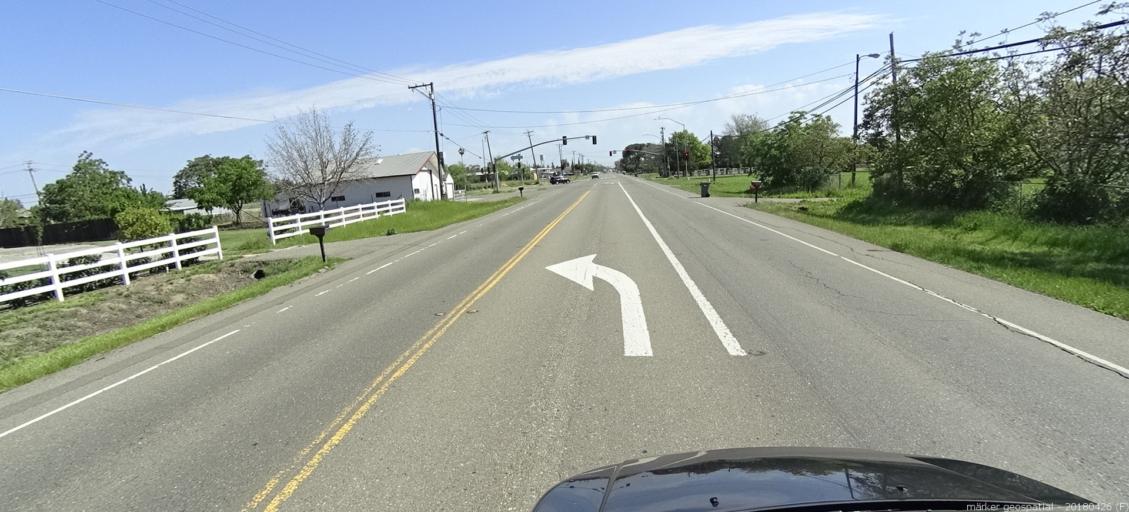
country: US
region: California
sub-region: Yolo County
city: West Sacramento
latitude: 38.5341
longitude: -121.5547
